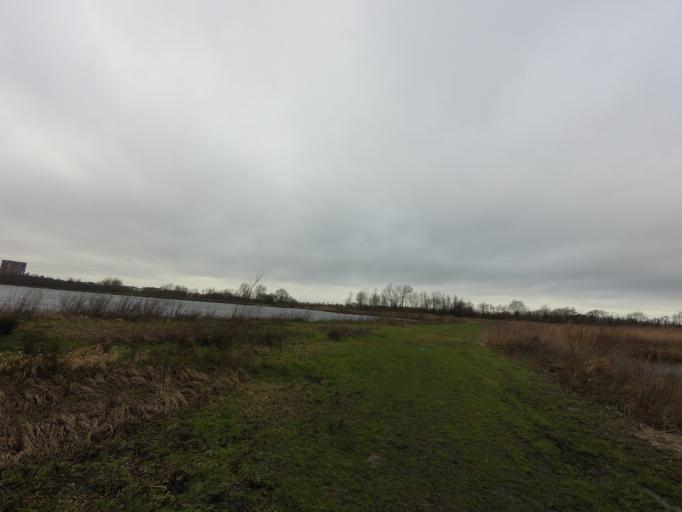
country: NL
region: Utrecht
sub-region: Gemeente Woerden
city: Woerden
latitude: 52.0877
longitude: 4.9260
